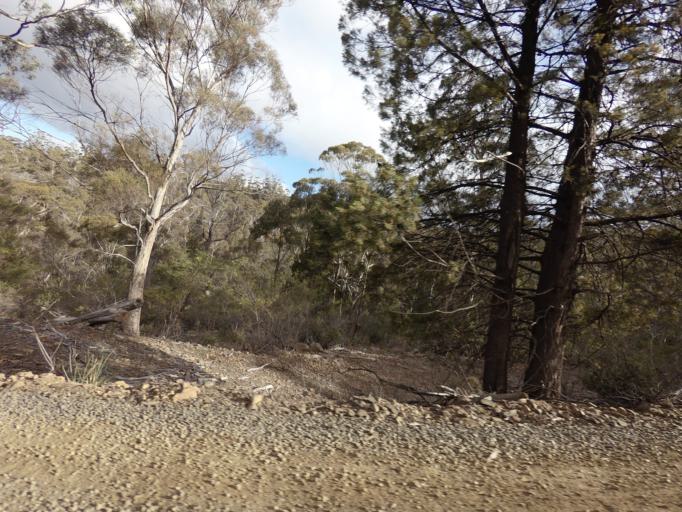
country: AU
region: Tasmania
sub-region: Sorell
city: Sorell
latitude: -42.2323
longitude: 148.0125
